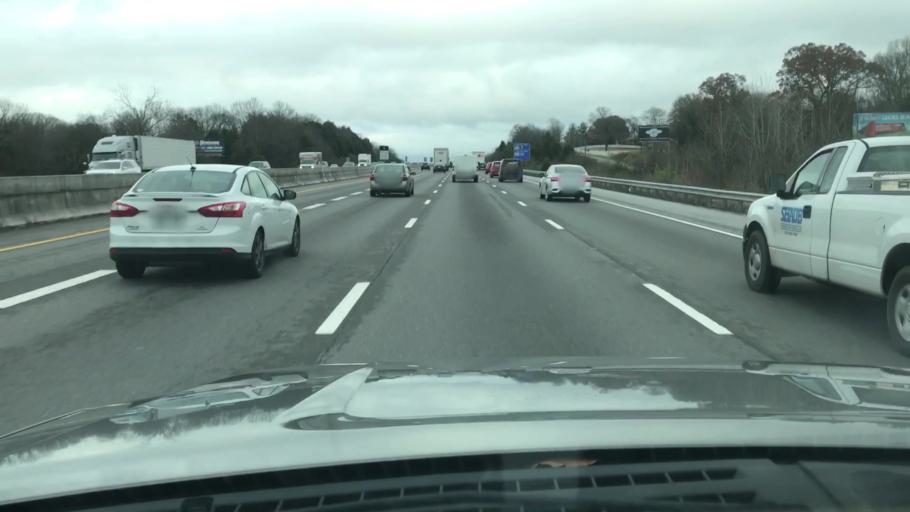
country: US
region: Tennessee
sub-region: Wilson County
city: Mount Juliet
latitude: 36.1673
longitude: -86.5423
